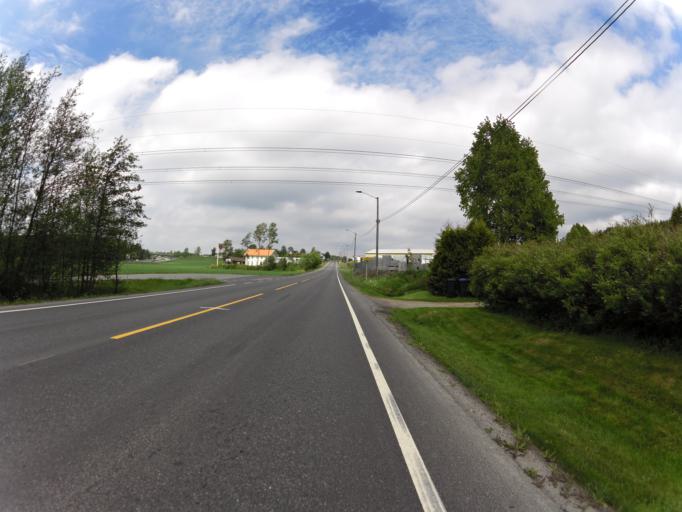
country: NO
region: Ostfold
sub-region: Rade
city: Karlshus
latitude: 59.3399
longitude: 10.9337
